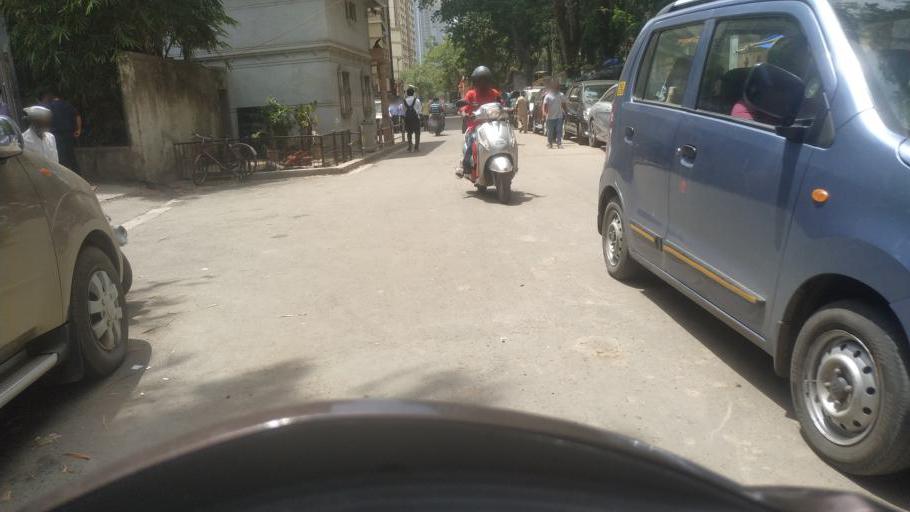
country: IN
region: Maharashtra
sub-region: Mumbai Suburban
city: Mumbai
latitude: 18.9998
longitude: 72.8261
